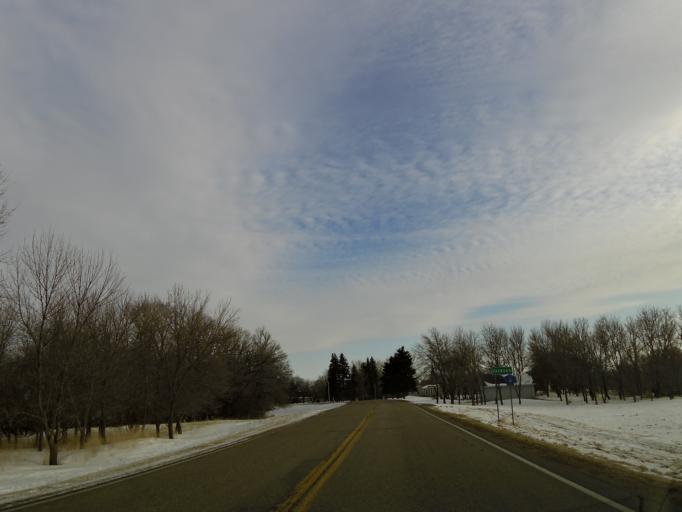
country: US
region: North Dakota
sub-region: Walsh County
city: Grafton
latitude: 48.4309
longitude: -97.2976
